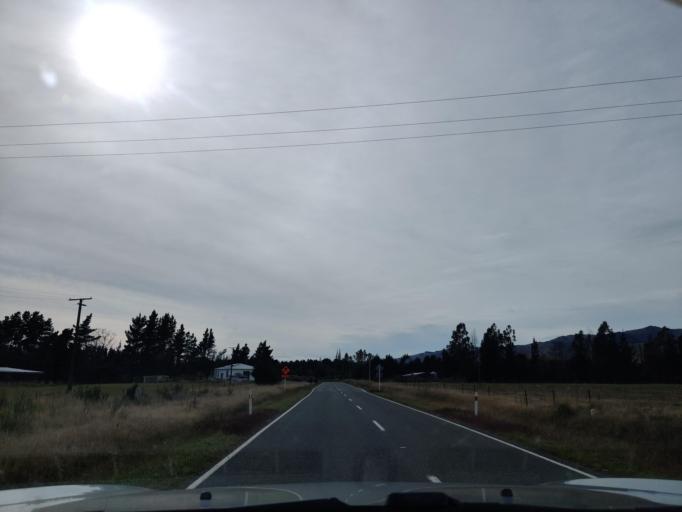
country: NZ
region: Tasman
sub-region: Tasman District
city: Brightwater
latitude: -41.6384
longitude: 173.3141
